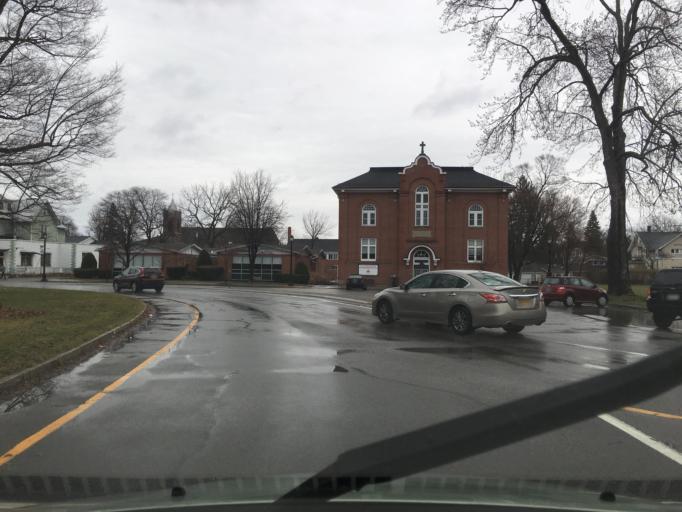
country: US
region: New York
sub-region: Livingston County
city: Avon
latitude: 42.9120
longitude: -77.7449
